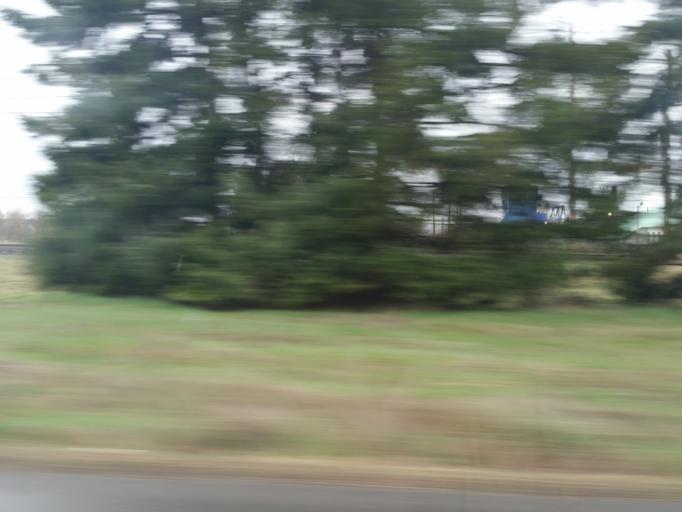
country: US
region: Washington
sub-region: Skagit County
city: Mount Vernon
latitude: 48.4463
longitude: -122.4389
